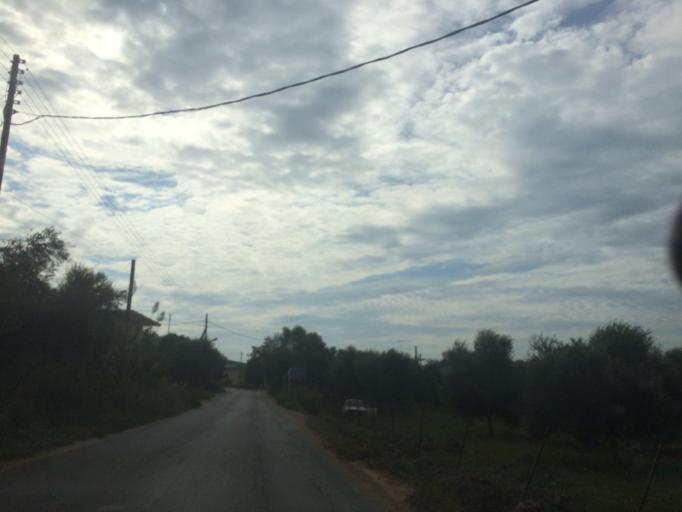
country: GR
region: Peloponnese
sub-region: Nomos Messinias
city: Pylos
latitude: 36.9627
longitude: 21.6971
